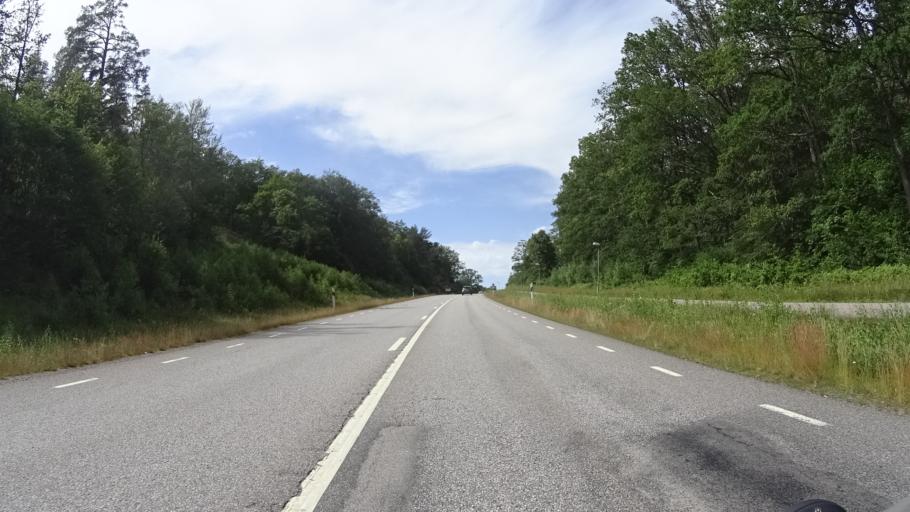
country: SE
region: Kalmar
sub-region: Vasterviks Kommun
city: Overum
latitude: 57.9844
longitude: 16.3191
